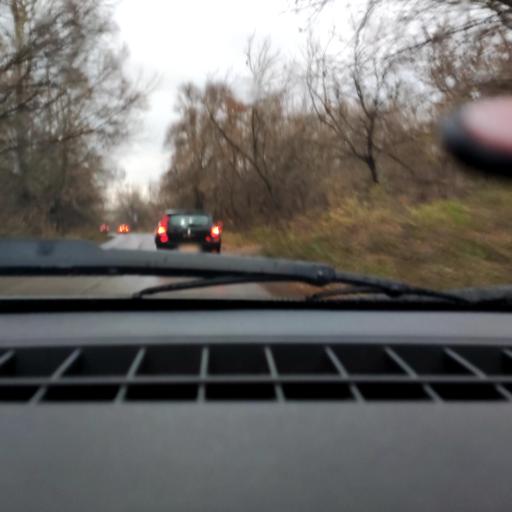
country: RU
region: Bashkortostan
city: Ufa
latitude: 54.8036
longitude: 56.1510
